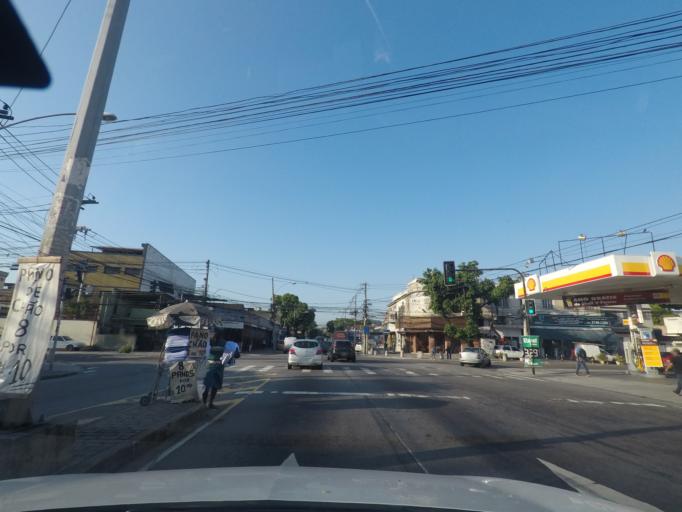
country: BR
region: Rio de Janeiro
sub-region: Duque De Caxias
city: Duque de Caxias
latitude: -22.8291
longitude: -43.2768
